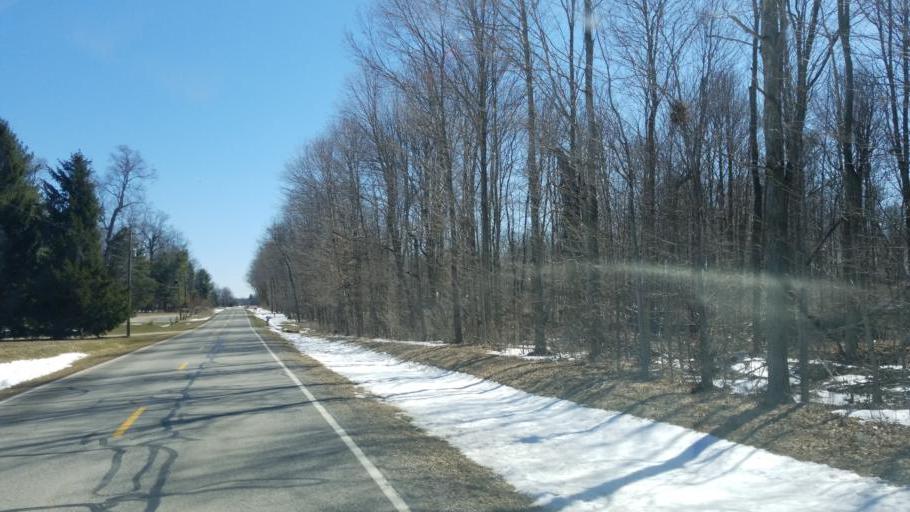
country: US
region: Ohio
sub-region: Crawford County
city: Bucyrus
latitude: 40.8046
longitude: -83.0244
